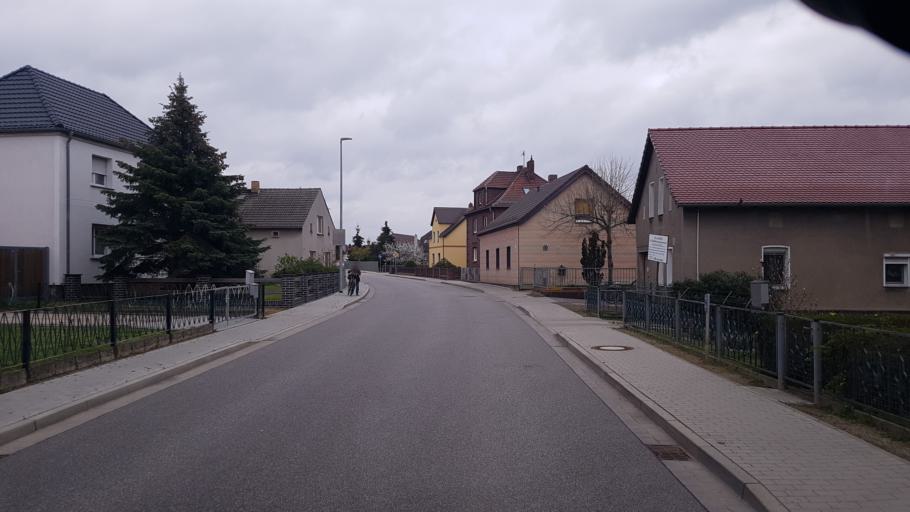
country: DE
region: Brandenburg
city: Hohenbocka
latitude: 51.4546
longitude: 14.0296
